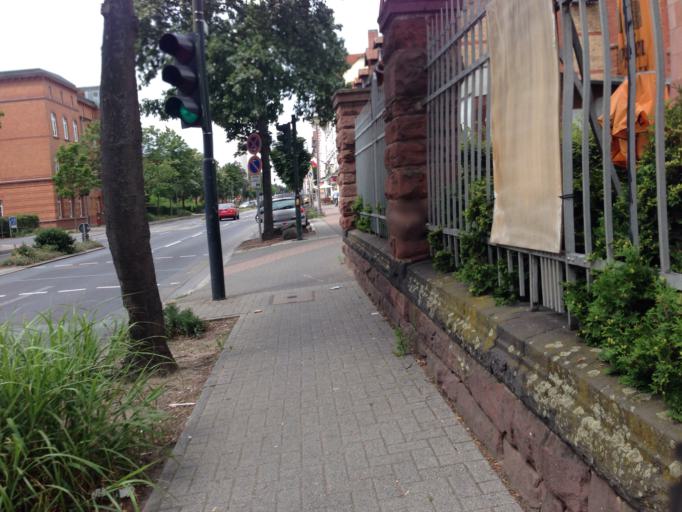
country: DE
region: Hesse
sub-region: Regierungsbezirk Darmstadt
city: Hanau am Main
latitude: 50.1425
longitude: 8.9354
